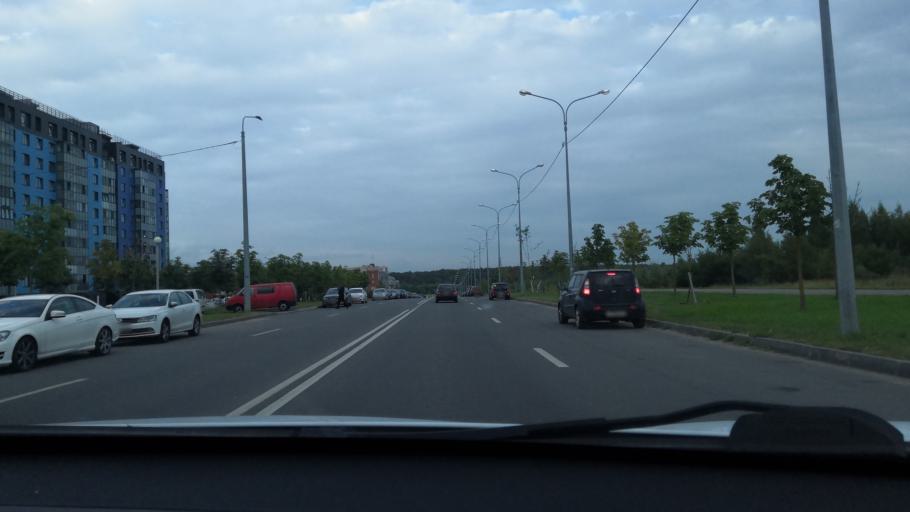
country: RU
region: St.-Petersburg
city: Pavlovsk
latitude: 59.6950
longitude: 30.4160
